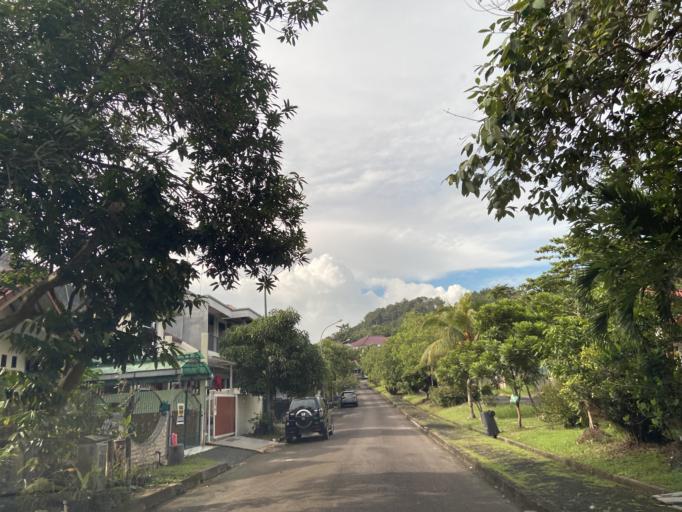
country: SG
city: Singapore
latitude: 1.1032
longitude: 104.0261
